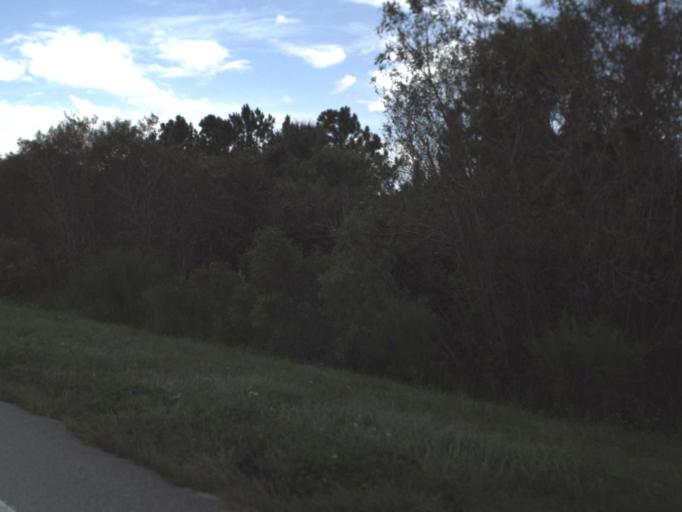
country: US
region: Florida
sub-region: Polk County
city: Babson Park
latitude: 27.8050
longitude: -81.2085
